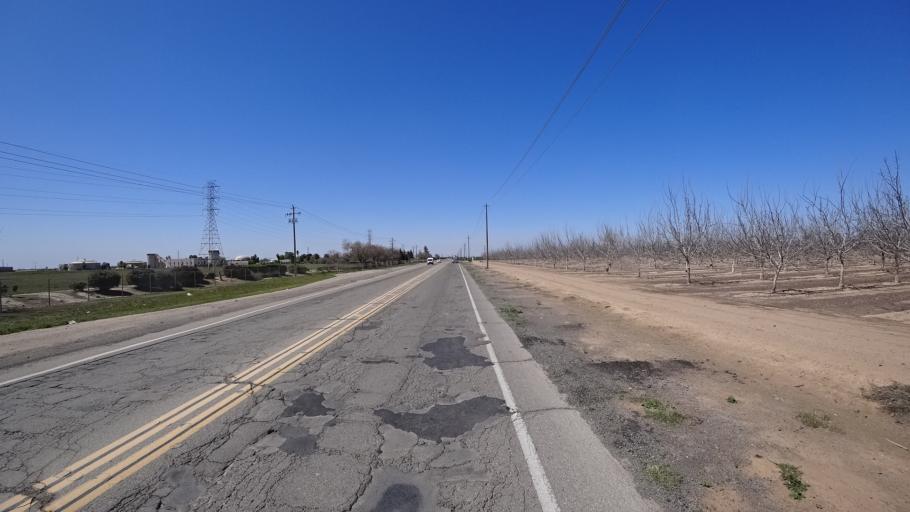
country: US
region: California
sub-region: Fresno County
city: West Park
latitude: 36.7064
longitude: -119.8869
